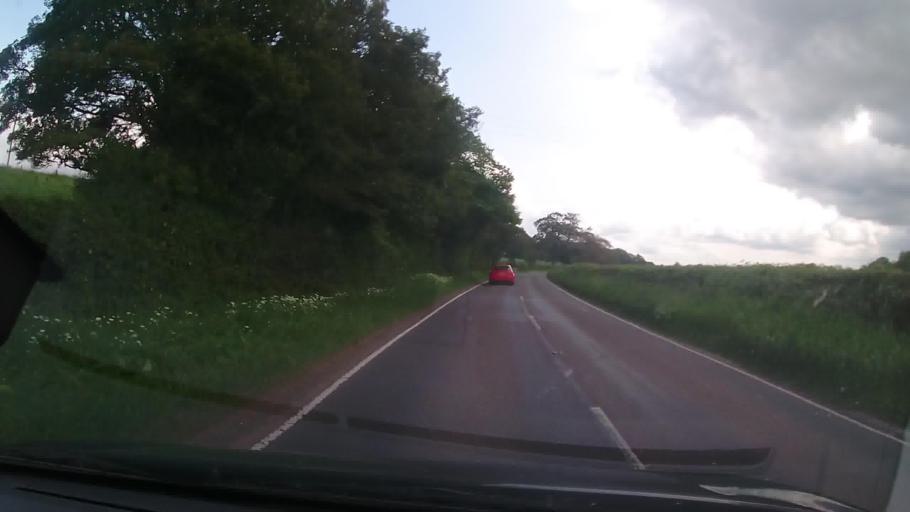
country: GB
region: England
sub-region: Shropshire
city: Wem
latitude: 52.8336
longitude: -2.7323
